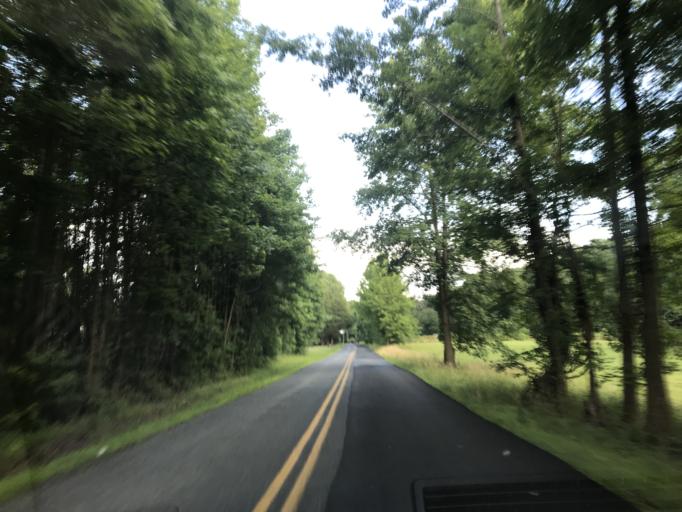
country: US
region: Maryland
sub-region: Harford County
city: Aberdeen
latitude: 39.5263
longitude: -76.2165
